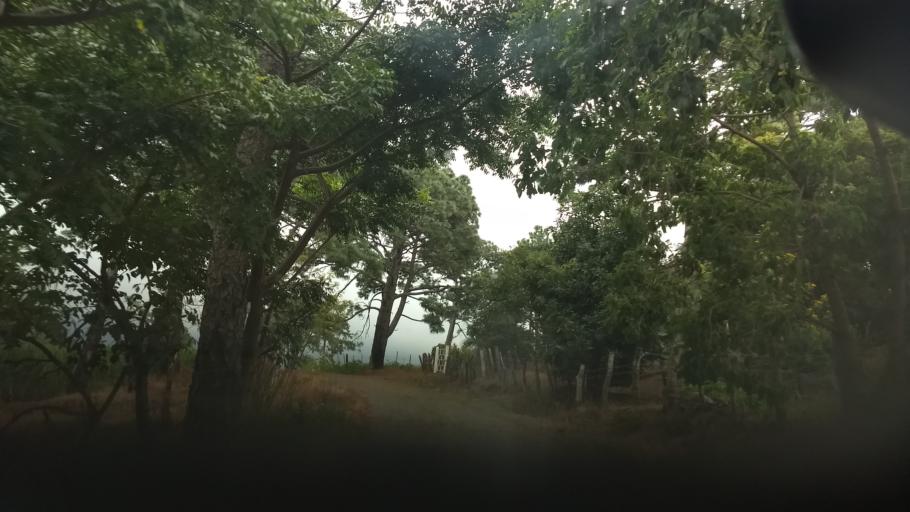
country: MX
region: Colima
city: Cofradia
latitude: 19.4688
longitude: -103.5389
